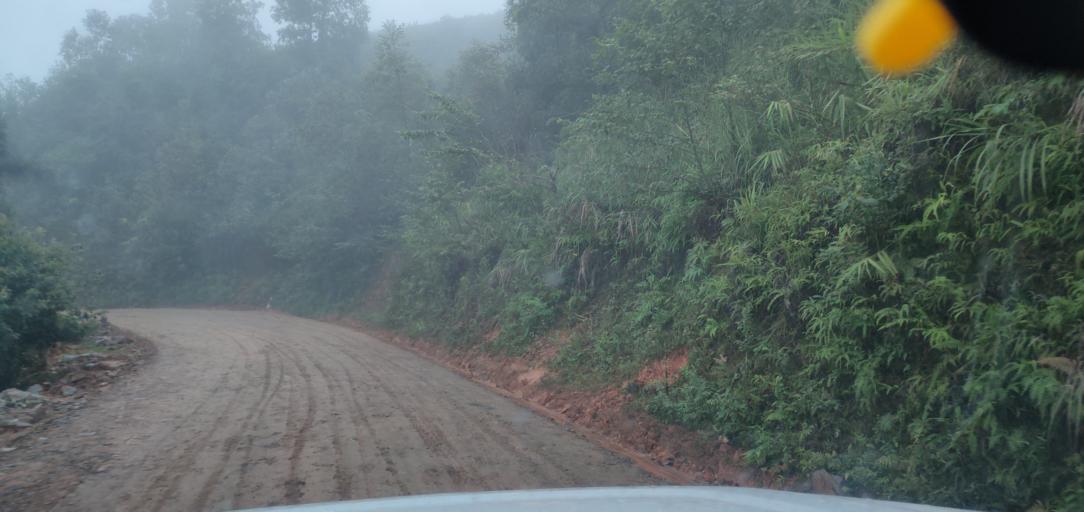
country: LA
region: Phongsali
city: Phongsali
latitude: 21.4282
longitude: 102.2596
